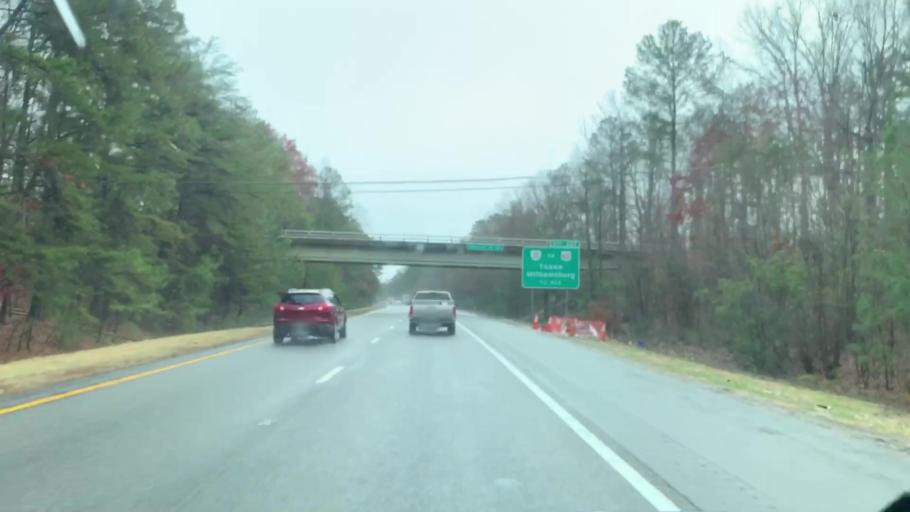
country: US
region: Virginia
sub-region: King William County
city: West Point
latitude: 37.4265
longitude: -76.8372
